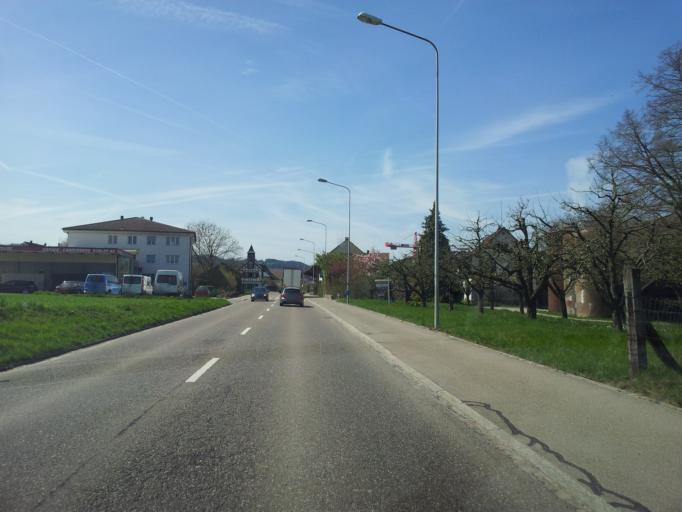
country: CH
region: Zurich
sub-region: Bezirk Dielsdorf
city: Otelfingen
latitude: 47.4462
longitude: 8.3897
